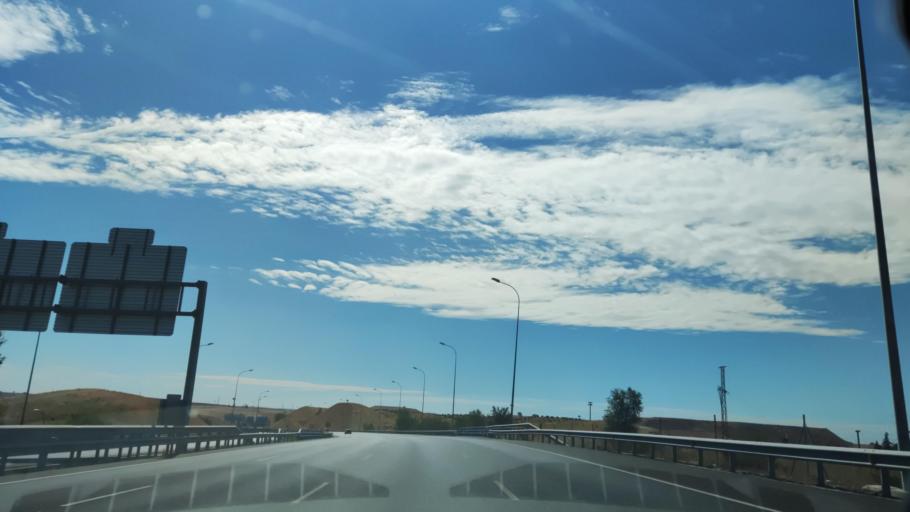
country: ES
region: Madrid
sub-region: Provincia de Madrid
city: Puente de Vallecas
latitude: 40.3685
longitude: -3.6500
